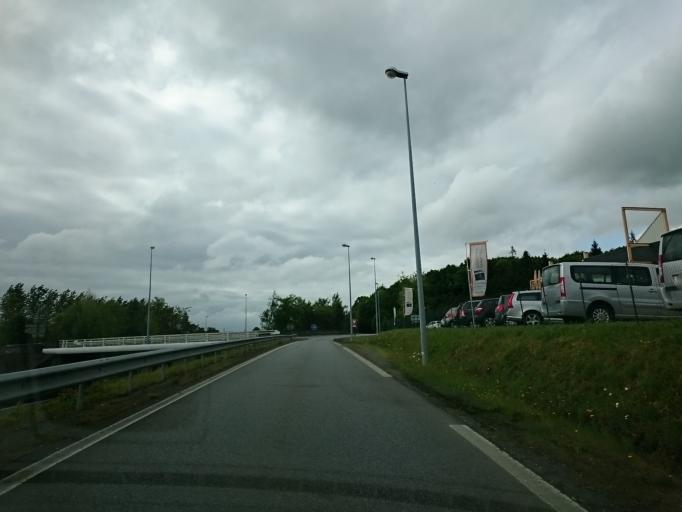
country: FR
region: Brittany
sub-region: Departement d'Ille-et-Vilaine
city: Vern-sur-Seiche
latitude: 48.0627
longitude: -1.6171
